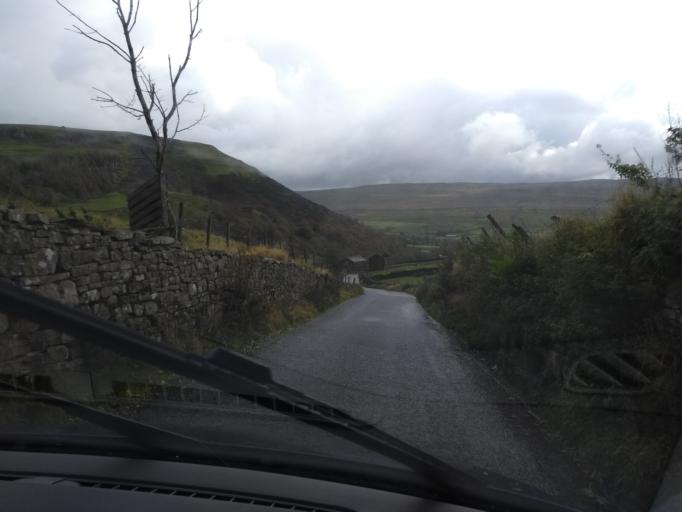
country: GB
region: England
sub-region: Cumbria
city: Kirkby Stephen
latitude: 54.3926
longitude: -2.1739
